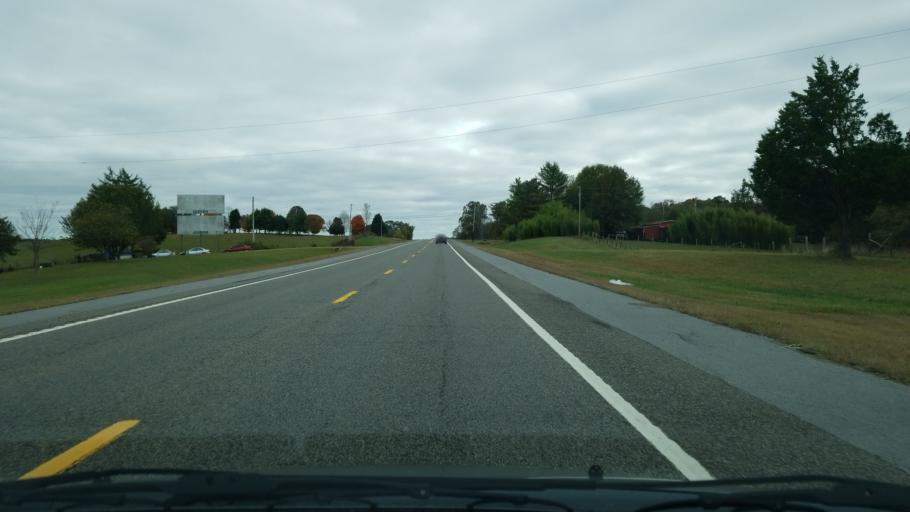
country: US
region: Tennessee
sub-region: Rhea County
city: Graysville
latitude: 35.3918
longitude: -85.0077
